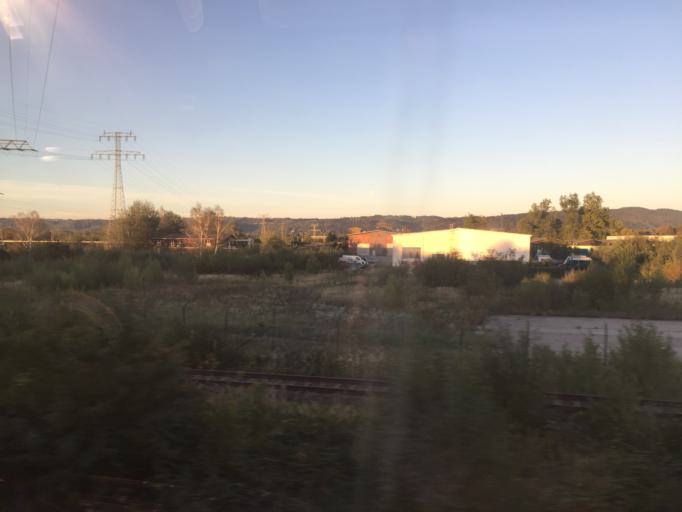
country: DE
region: Saxony
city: Heidenau
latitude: 50.9920
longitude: 13.8411
